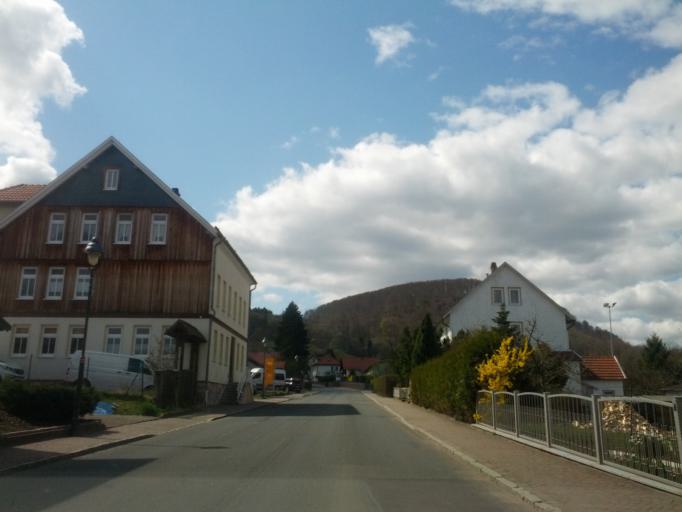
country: DE
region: Thuringia
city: Seebach
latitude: 50.9001
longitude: 10.4490
